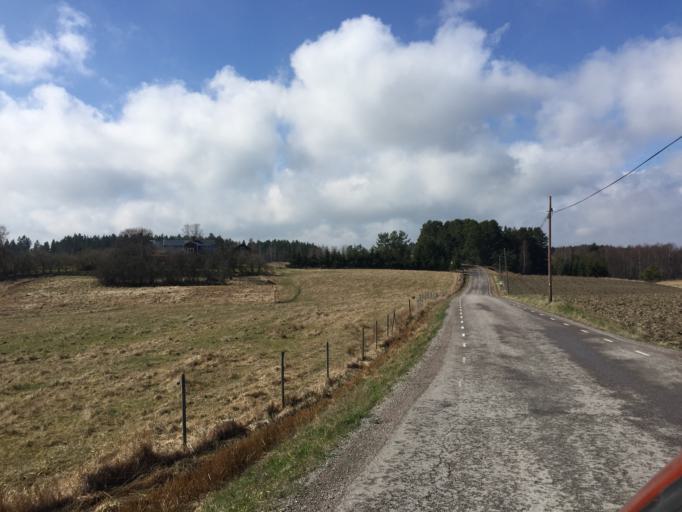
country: SE
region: Soedermanland
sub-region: Gnesta Kommun
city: Gnesta
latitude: 59.0355
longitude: 17.2283
